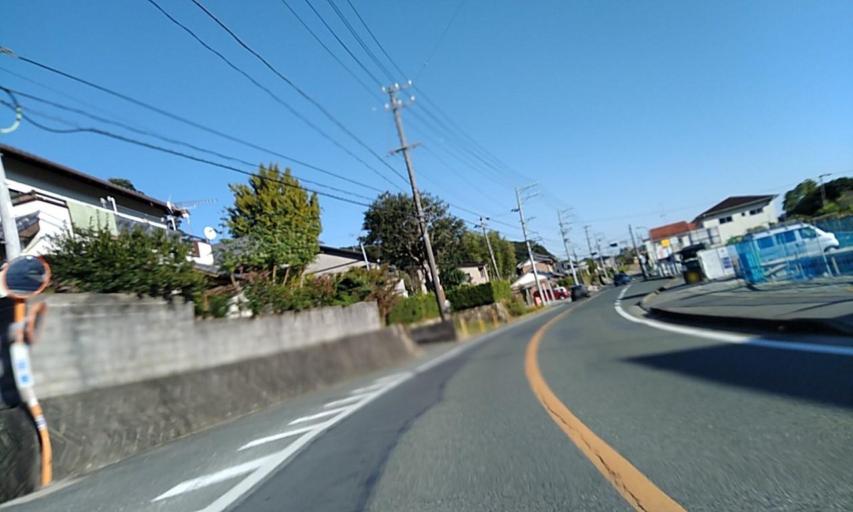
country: JP
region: Shizuoka
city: Hamakita
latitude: 34.8368
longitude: 137.6626
